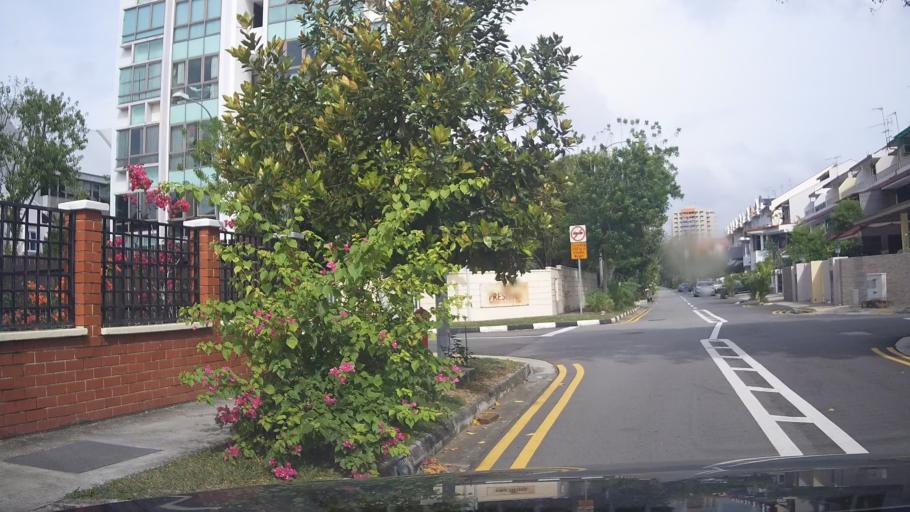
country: SG
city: Singapore
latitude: 1.3105
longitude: 103.9000
